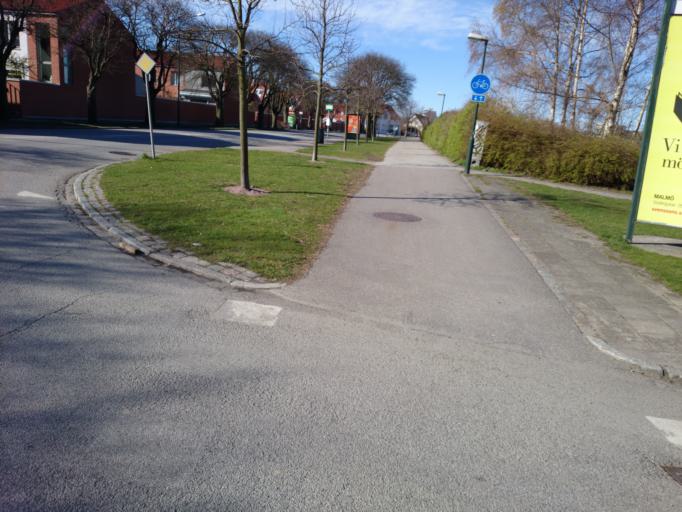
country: SE
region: Skane
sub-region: Malmo
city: Bunkeflostrand
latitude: 55.5879
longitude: 12.9370
